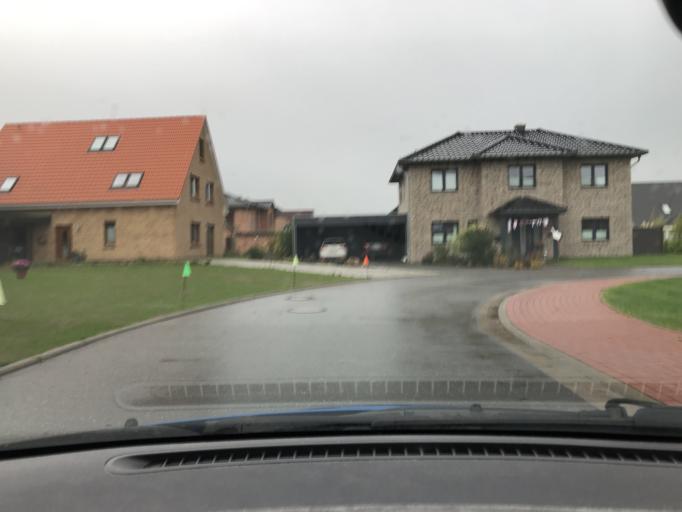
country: DE
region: Schleswig-Holstein
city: Fahrdorf
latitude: 54.5038
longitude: 9.6150
